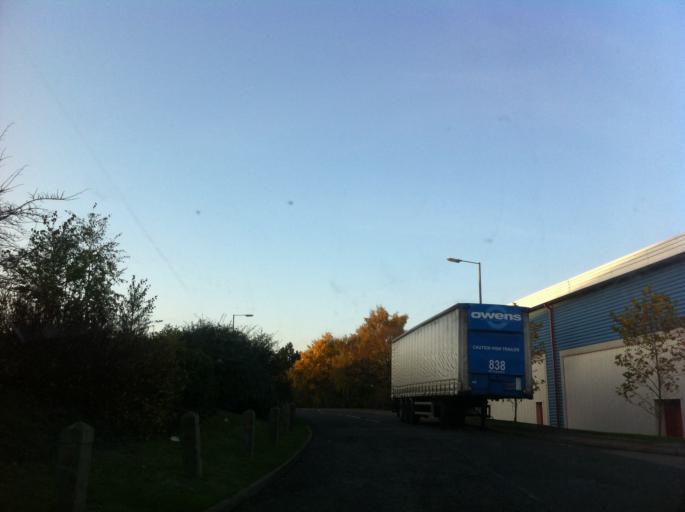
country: GB
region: England
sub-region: Northamptonshire
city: Kettering
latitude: 52.3743
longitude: -0.7086
